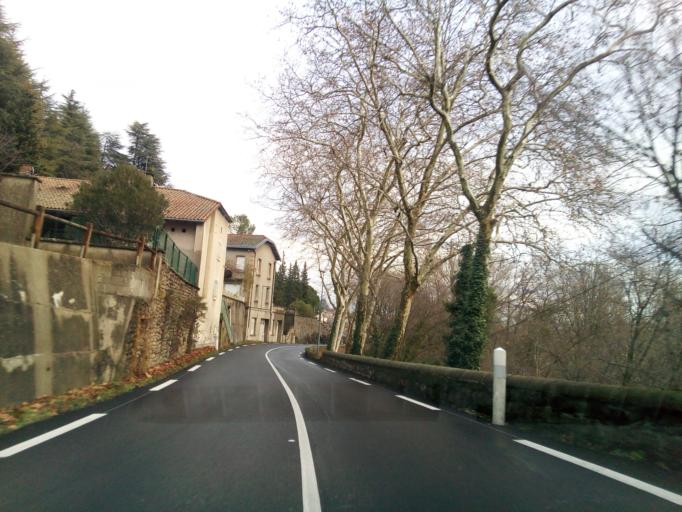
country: FR
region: Rhone-Alpes
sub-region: Departement de l'Ardeche
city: Beauchastel
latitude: 44.8282
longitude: 4.7867
